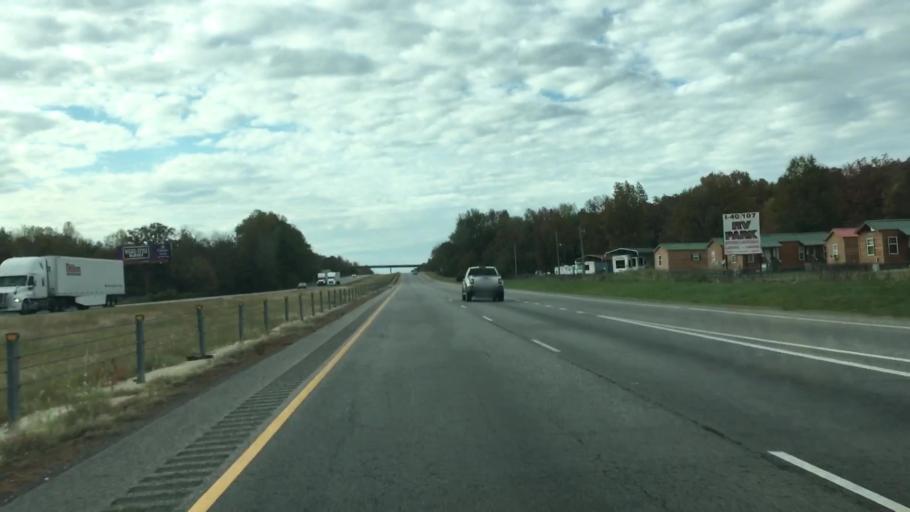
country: US
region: Arkansas
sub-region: Conway County
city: Morrilton
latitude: 35.1767
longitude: -92.7488
